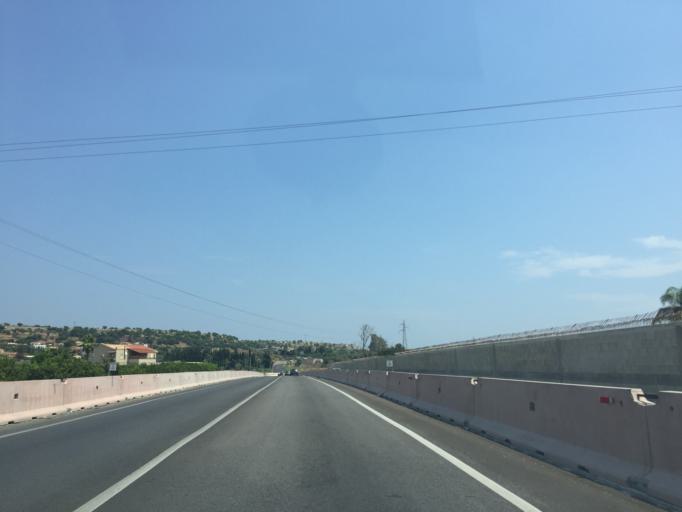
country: IT
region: Sicily
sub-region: Provincia di Siracusa
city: Siracusa
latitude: 37.0740
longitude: 15.2444
